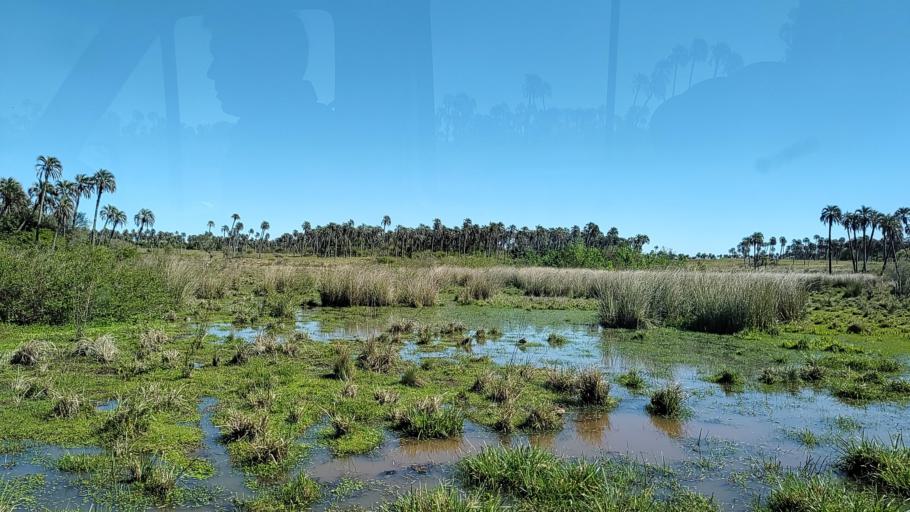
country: AR
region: Entre Rios
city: Ubajay
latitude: -31.8857
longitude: -58.2383
